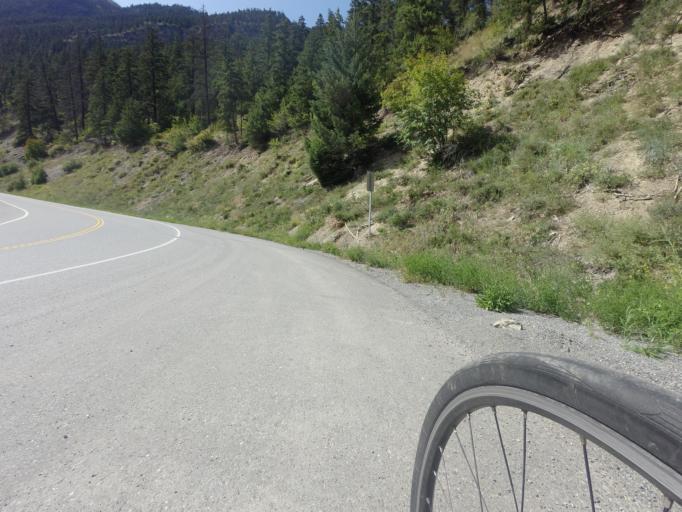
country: CA
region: British Columbia
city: Lillooet
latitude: 50.6550
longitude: -122.0079
